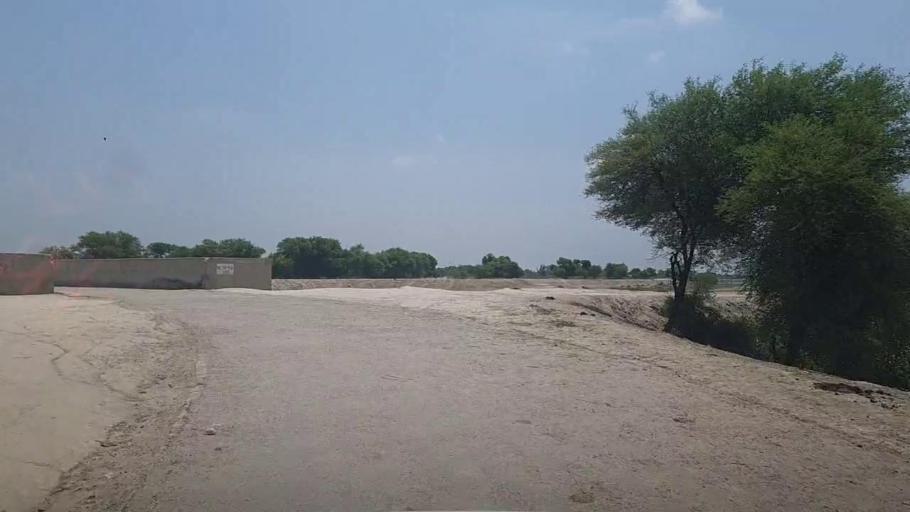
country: PK
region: Sindh
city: Ubauro
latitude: 28.2427
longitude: 69.8288
